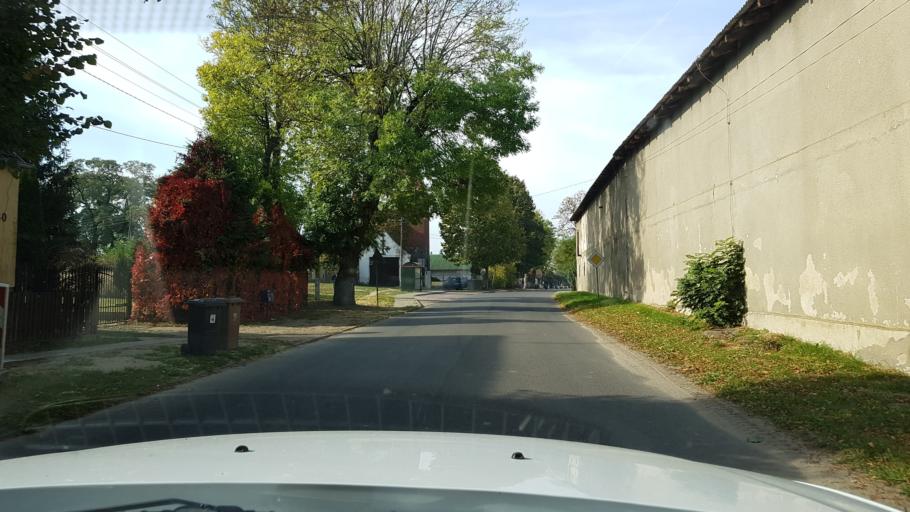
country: PL
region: West Pomeranian Voivodeship
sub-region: Powiat mysliborski
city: Barlinek
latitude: 52.9597
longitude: 15.1231
